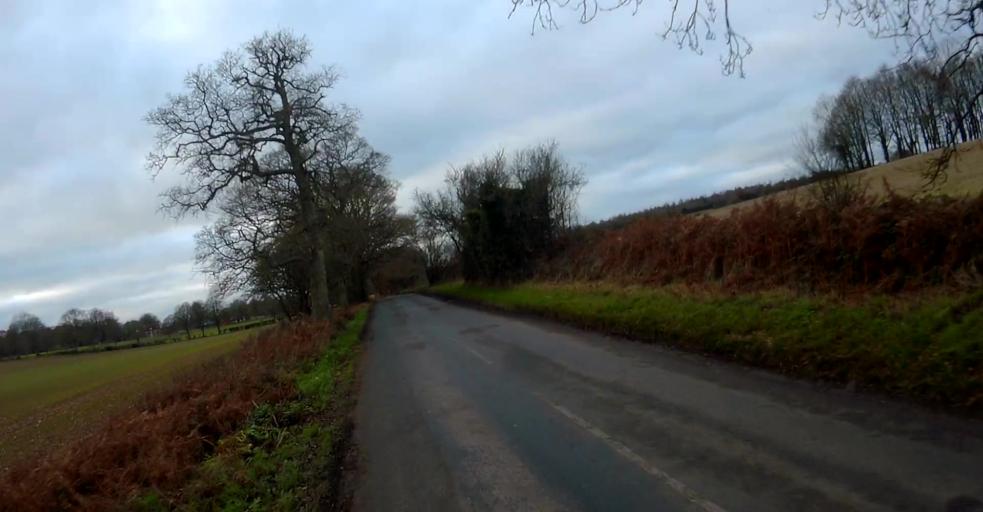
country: GB
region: England
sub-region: Hampshire
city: Overton
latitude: 51.1986
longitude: -1.1694
